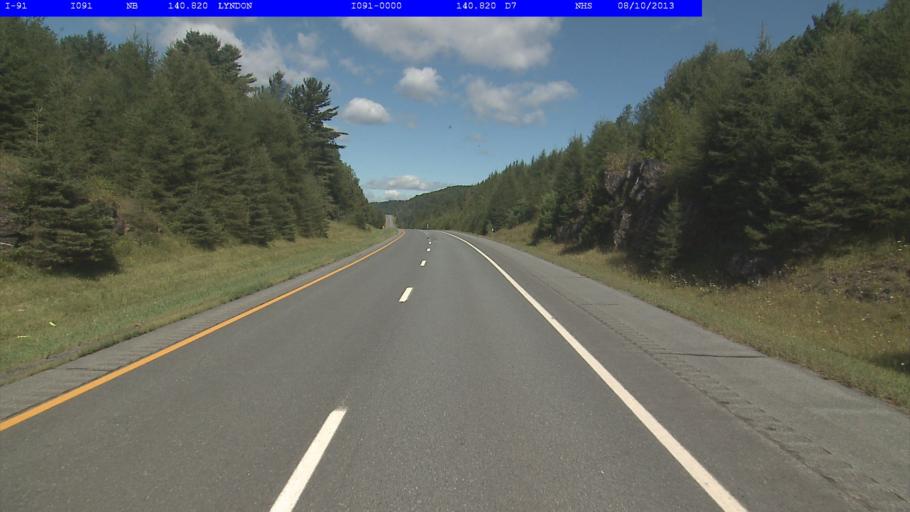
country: US
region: Vermont
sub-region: Caledonia County
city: Lyndonville
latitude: 44.5659
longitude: -72.0316
